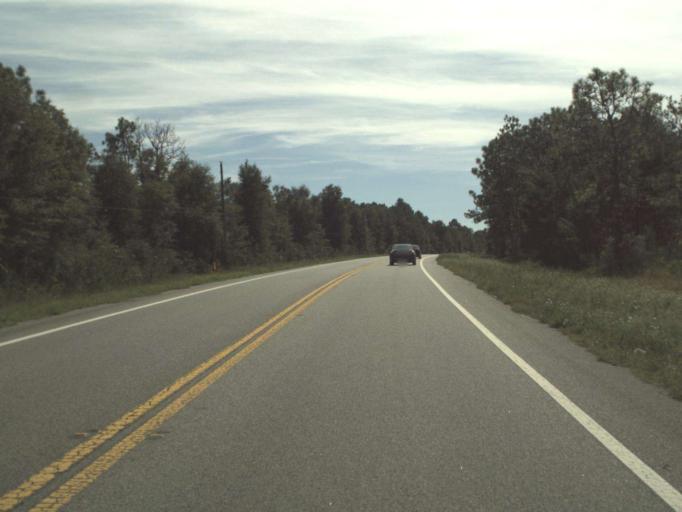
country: US
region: Florida
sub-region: Washington County
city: Chipley
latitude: 30.5931
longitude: -85.5925
